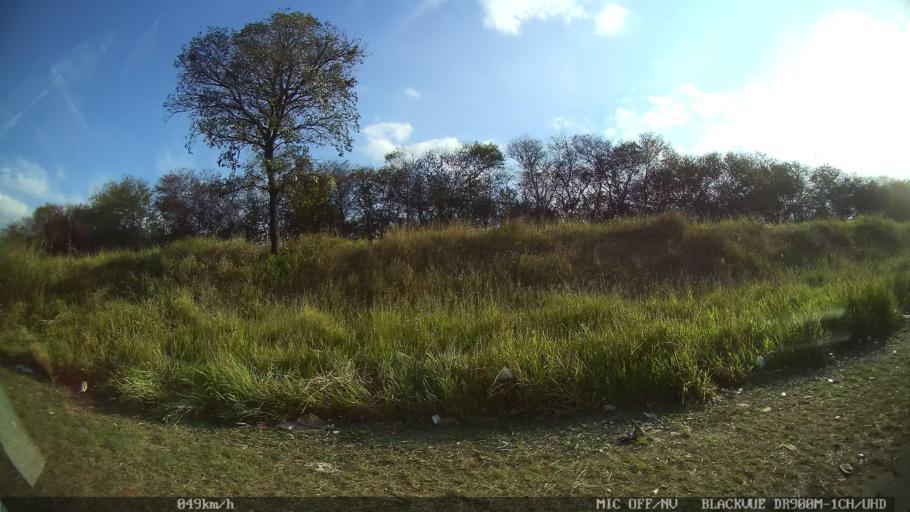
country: BR
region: Sao Paulo
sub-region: Hortolandia
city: Hortolandia
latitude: -22.8757
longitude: -47.1537
